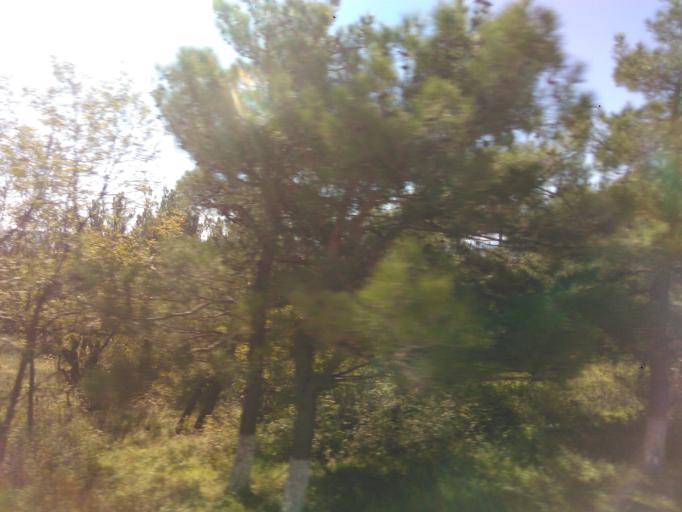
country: RU
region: Krasnodarskiy
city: Gelendzhik
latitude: 44.6000
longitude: 38.0361
